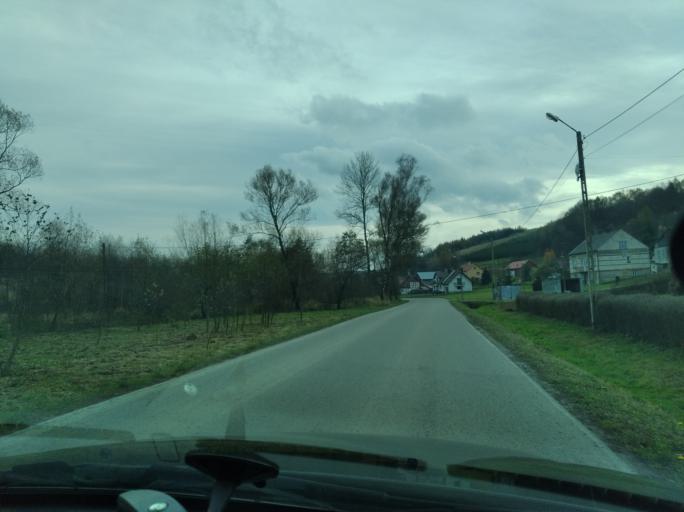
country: PL
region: Subcarpathian Voivodeship
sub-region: Powiat strzyzowski
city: Strzyzow
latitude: 49.9441
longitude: 21.7513
